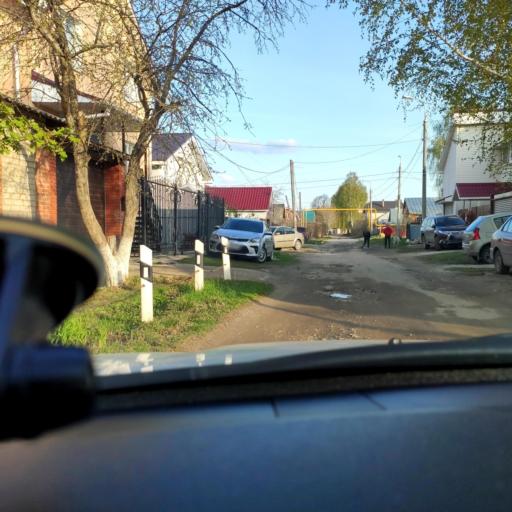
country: RU
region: Samara
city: Volzhskiy
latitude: 53.3558
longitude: 50.2156
